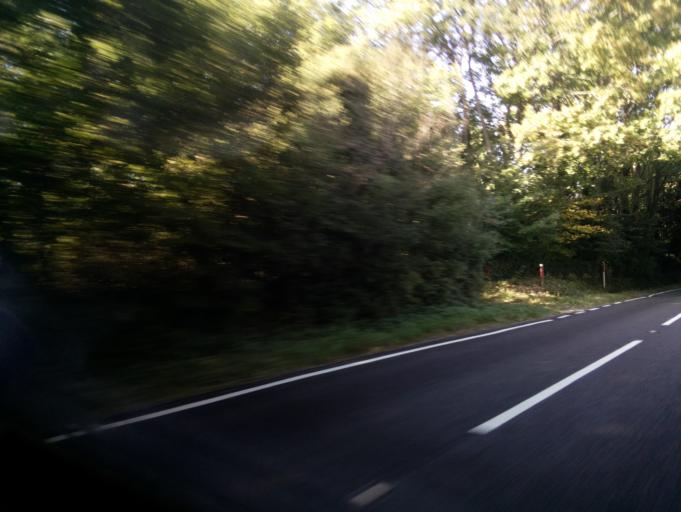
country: GB
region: England
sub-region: Hampshire
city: Four Marks
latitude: 51.0284
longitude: -1.0760
